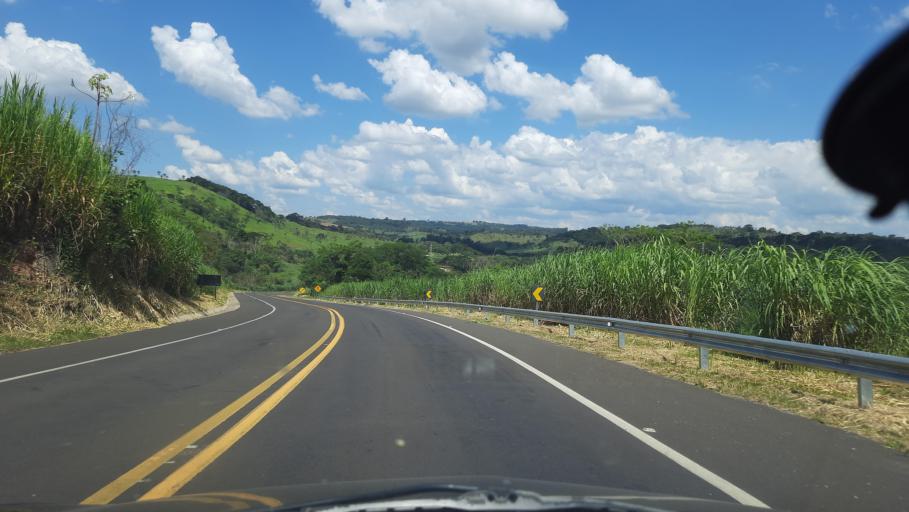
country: BR
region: Sao Paulo
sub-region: Sao Jose Do Rio Pardo
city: Sao Jose do Rio Pardo
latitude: -21.6038
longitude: -46.9756
